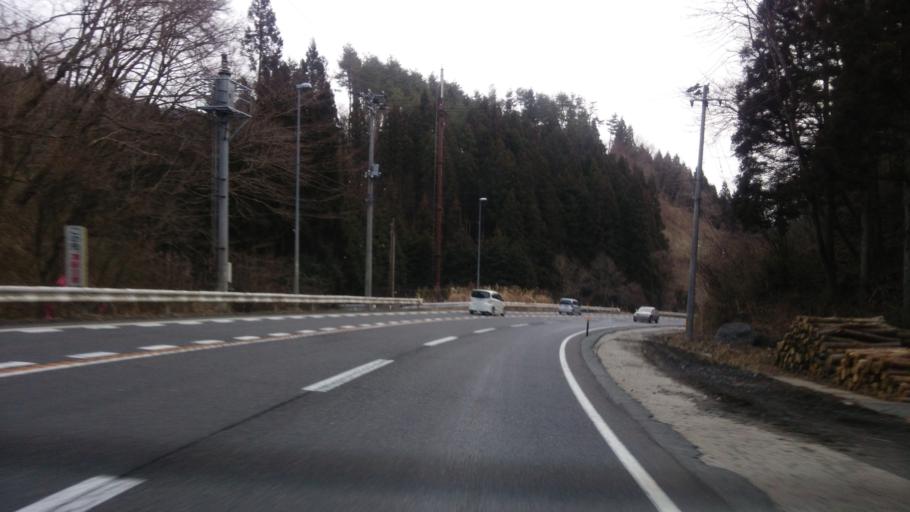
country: JP
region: Fukushima
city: Ishikawa
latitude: 37.1655
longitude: 140.6582
